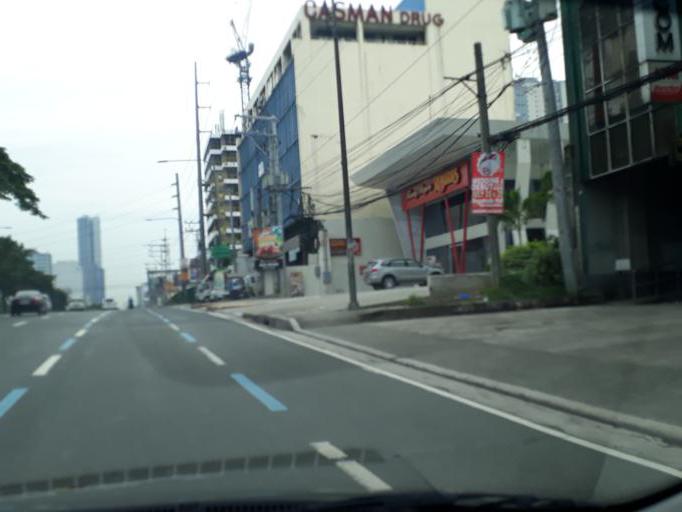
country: PH
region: Calabarzon
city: Del Monte
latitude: 14.6357
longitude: 121.0241
